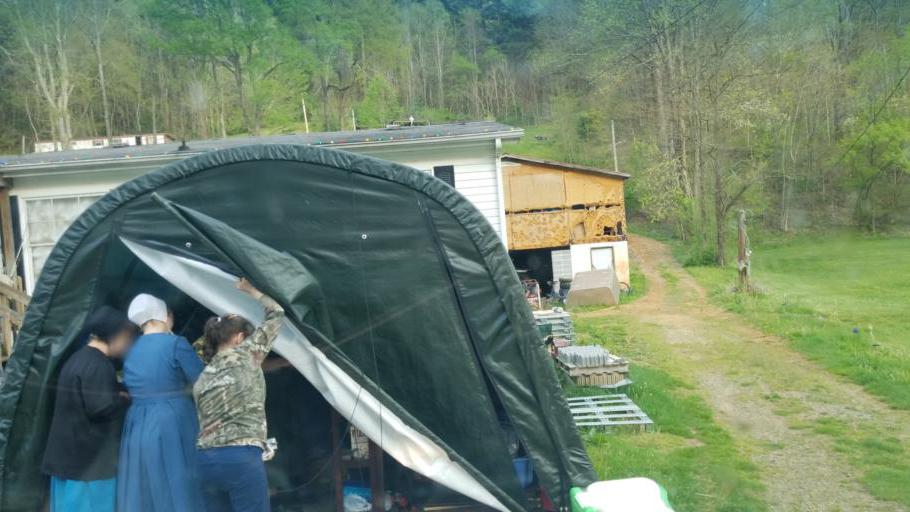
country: US
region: Virginia
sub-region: Smyth County
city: Marion
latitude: 36.8081
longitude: -81.4668
